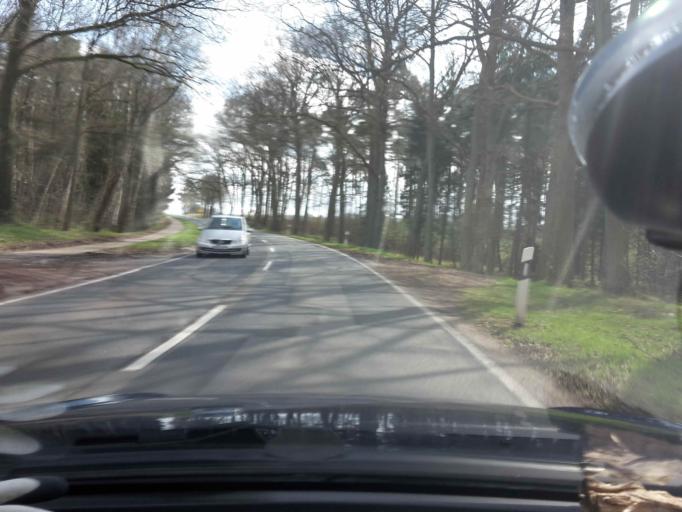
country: DE
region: Lower Saxony
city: Jesteburg
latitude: 53.2992
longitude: 9.9614
